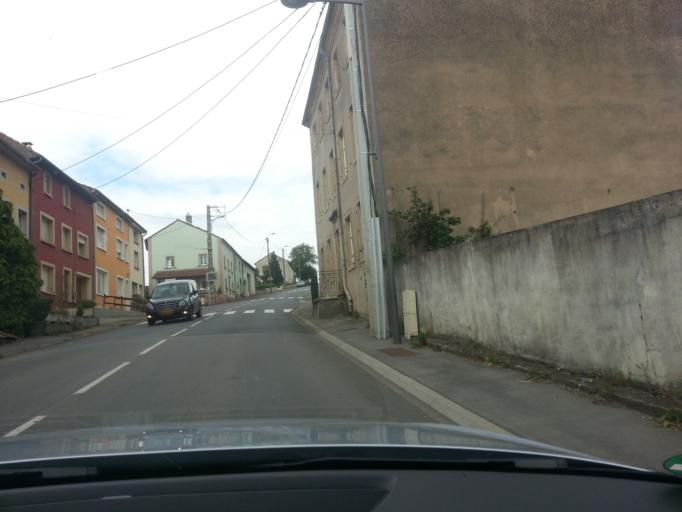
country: DE
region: Saarland
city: Perl
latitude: 49.4601
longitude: 6.3742
